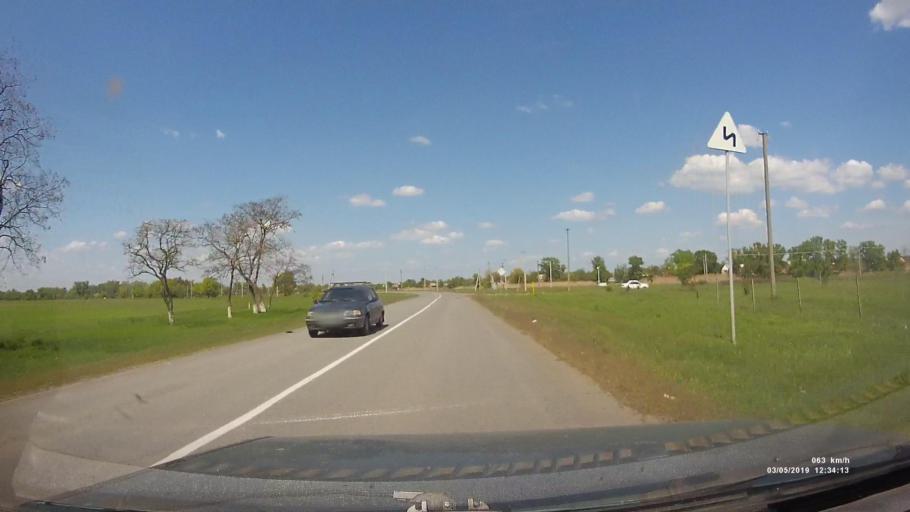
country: RU
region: Rostov
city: Semikarakorsk
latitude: 47.5204
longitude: 40.7691
